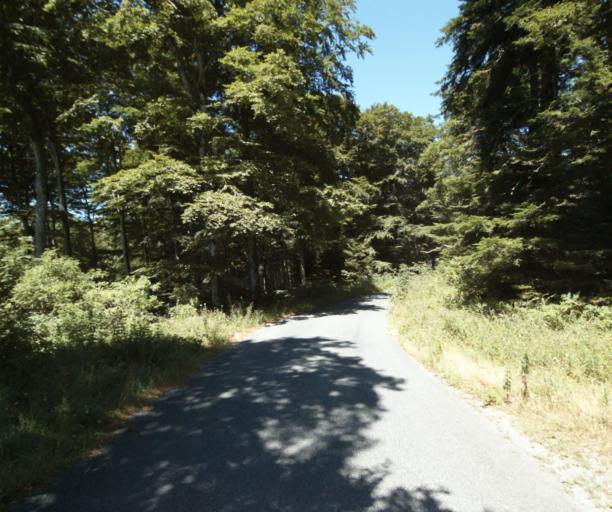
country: FR
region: Midi-Pyrenees
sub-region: Departement du Tarn
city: Dourgne
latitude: 43.4104
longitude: 2.1890
